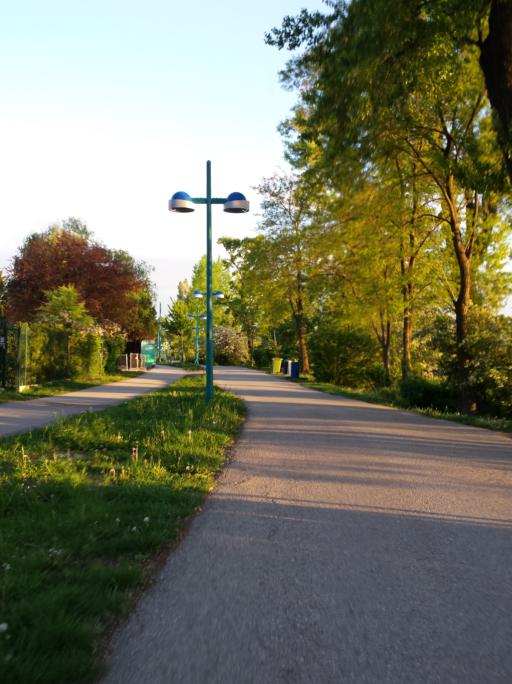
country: AT
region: Vienna
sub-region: Wien Stadt
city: Vienna
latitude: 48.2188
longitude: 16.4365
